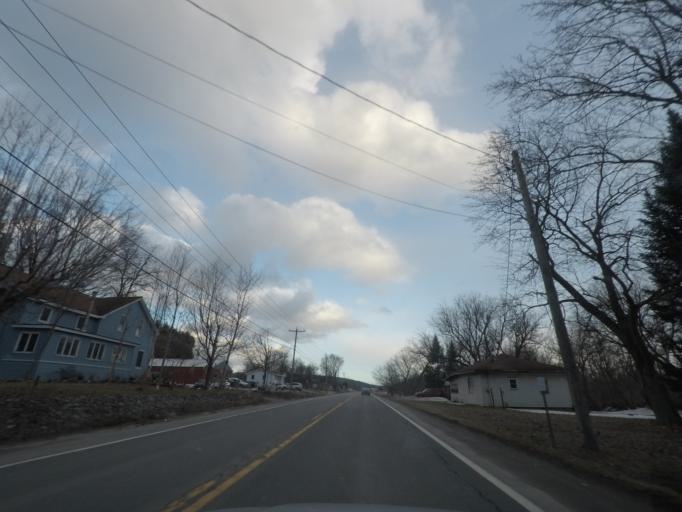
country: US
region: New York
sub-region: Herkimer County
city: Frankfort
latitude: 43.0626
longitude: -75.0890
